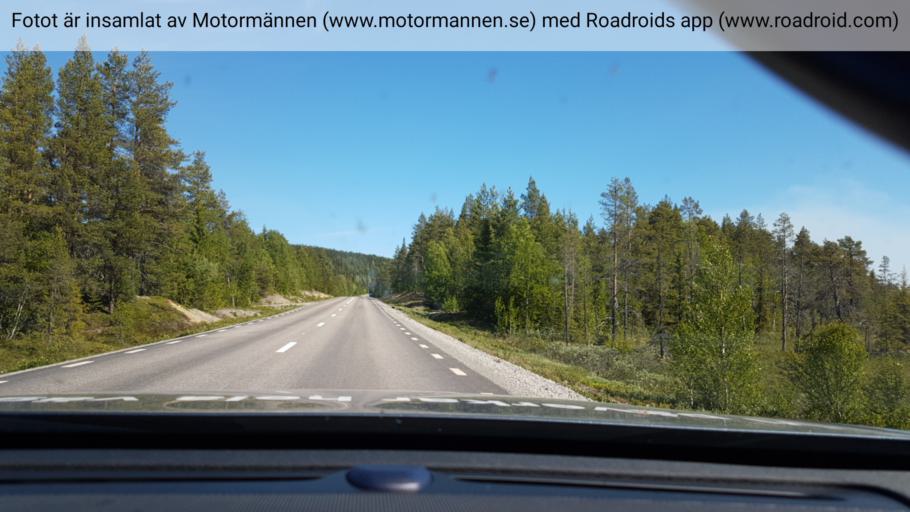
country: SE
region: Vaesterbotten
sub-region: Asele Kommun
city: Insjon
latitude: 64.7212
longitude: 17.6447
